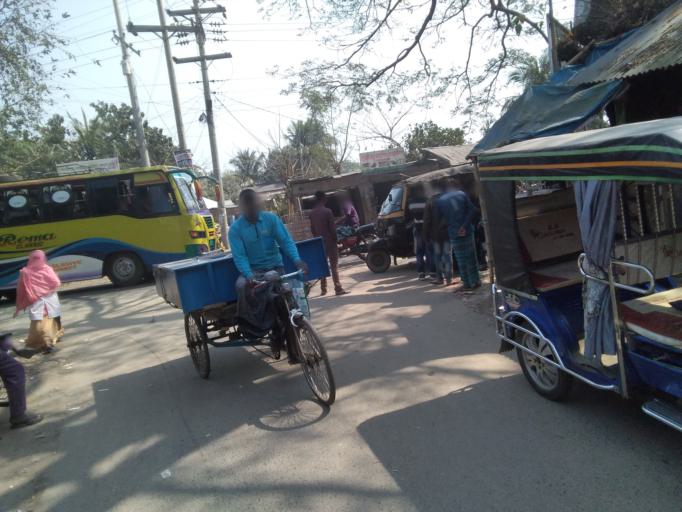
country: IN
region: West Bengal
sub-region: North 24 Parganas
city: Taki
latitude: 22.5899
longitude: 88.9996
